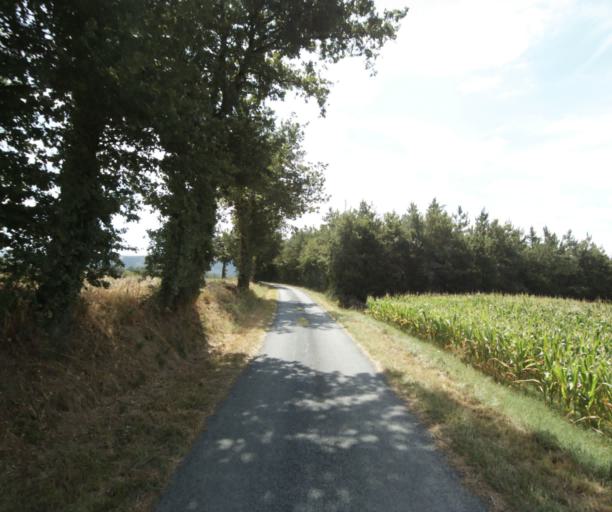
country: FR
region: Midi-Pyrenees
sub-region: Departement du Tarn
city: Dourgne
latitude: 43.4907
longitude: 2.0971
